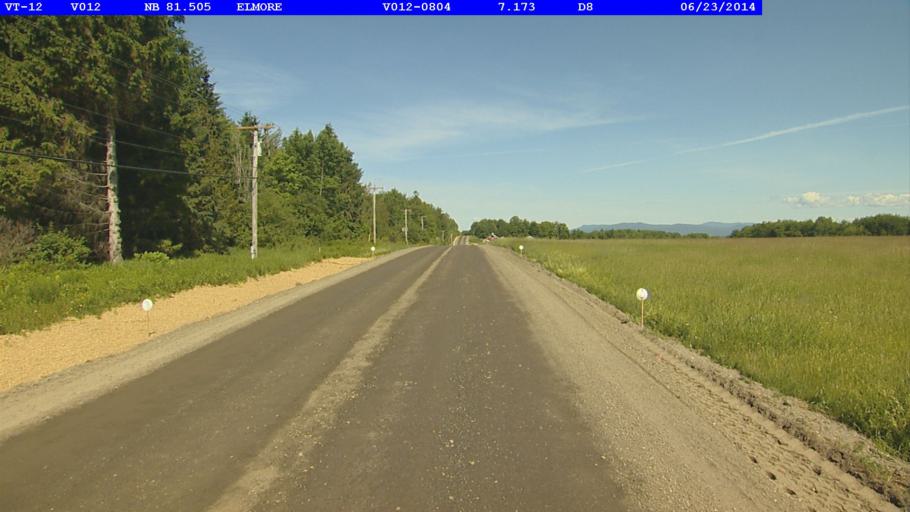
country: US
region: Vermont
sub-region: Lamoille County
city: Morrisville
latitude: 44.5455
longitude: -72.5288
